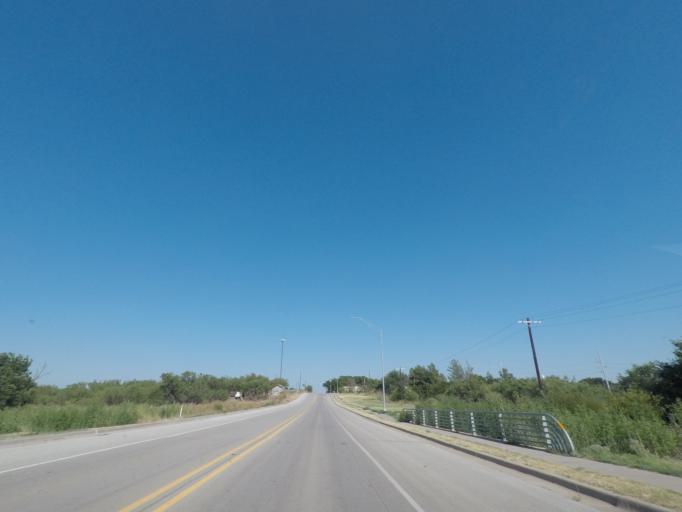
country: US
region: Texas
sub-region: Baylor County
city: Seymour
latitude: 33.5961
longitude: -99.2539
